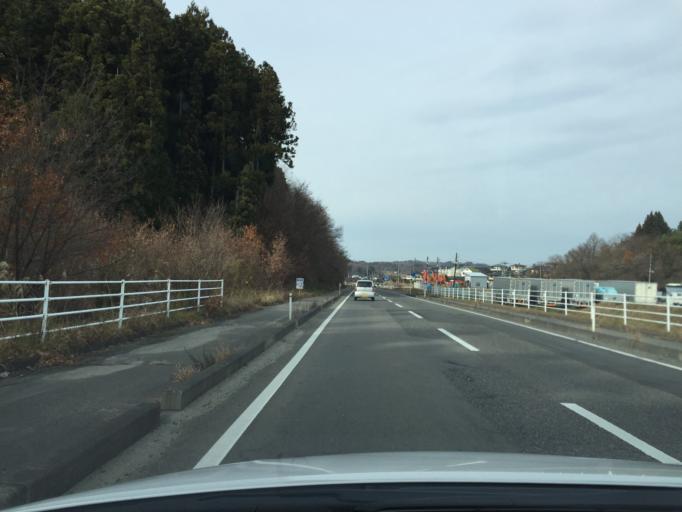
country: JP
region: Fukushima
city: Funehikimachi-funehiki
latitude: 37.4515
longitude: 140.5792
